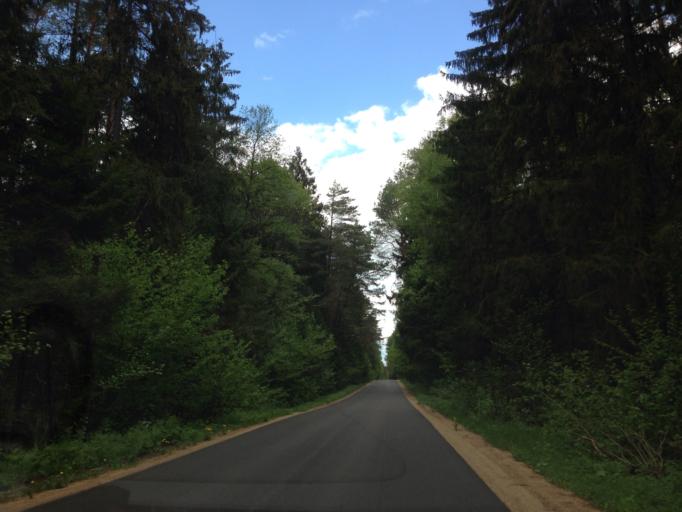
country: PL
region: Podlasie
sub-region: Powiat grajewski
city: Radzilow
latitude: 53.3406
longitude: 22.5982
